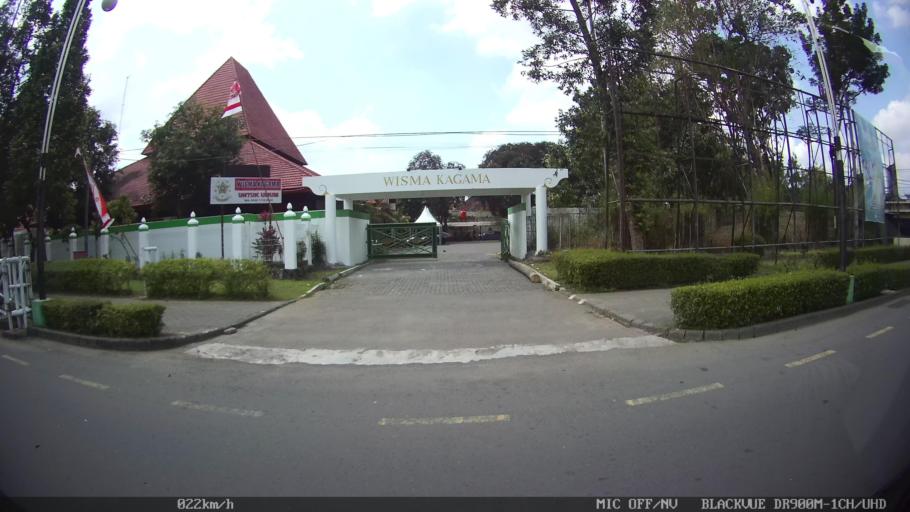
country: ID
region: Daerah Istimewa Yogyakarta
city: Yogyakarta
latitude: -7.7754
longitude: 110.3765
